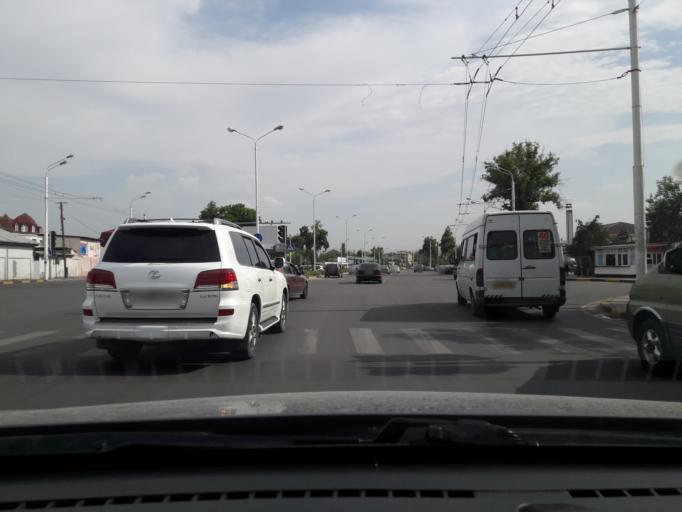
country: TJ
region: Dushanbe
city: Dushanbe
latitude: 38.5409
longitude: 68.7552
